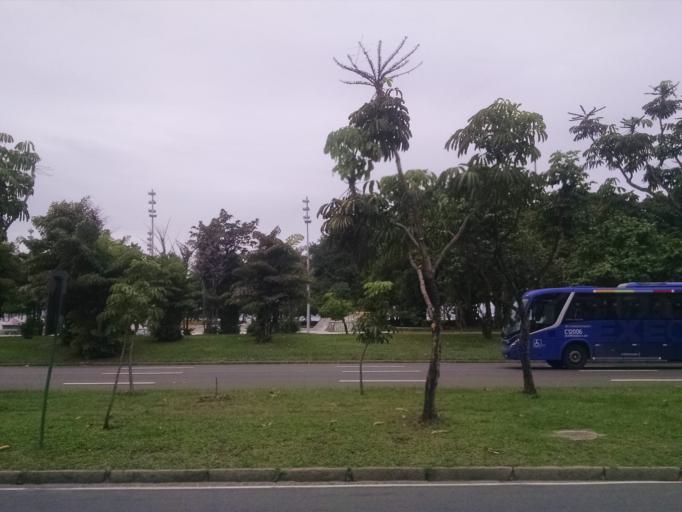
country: BR
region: Rio de Janeiro
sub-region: Rio De Janeiro
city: Rio de Janeiro
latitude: -22.9241
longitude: -43.1712
